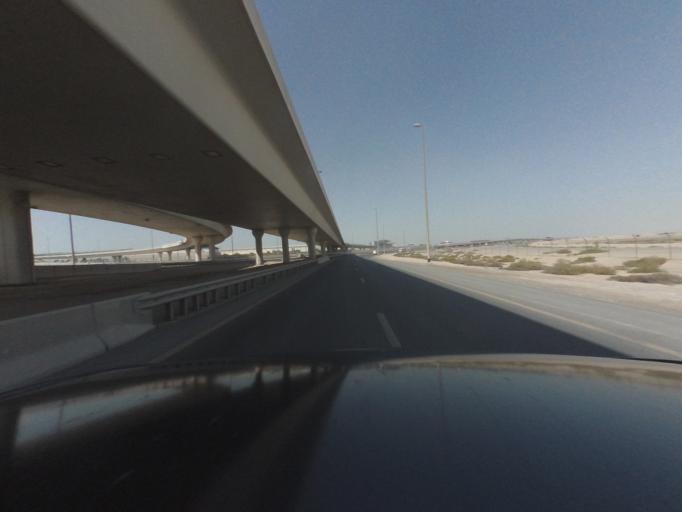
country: AE
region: Dubai
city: Dubai
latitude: 24.9894
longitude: 55.0951
